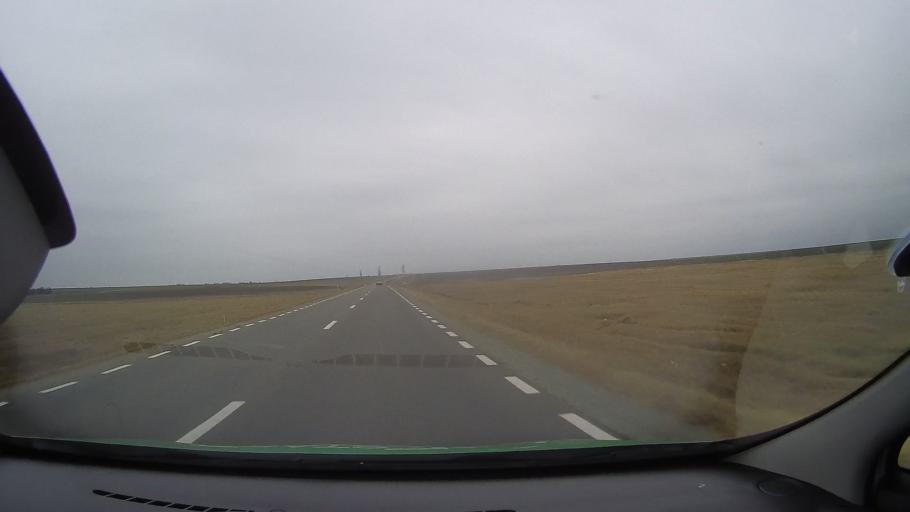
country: RO
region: Ialomita
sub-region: Comuna Scanteia
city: Iazu
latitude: 44.7225
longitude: 27.4223
